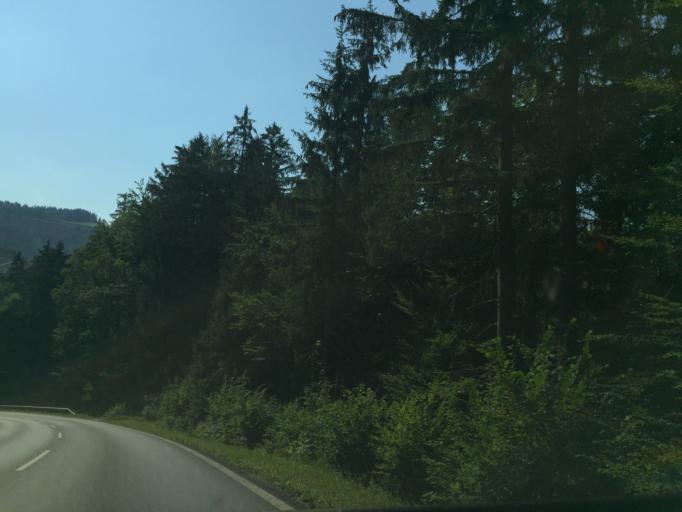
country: AT
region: Styria
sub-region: Politischer Bezirk Deutschlandsberg
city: Aibl
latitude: 46.6497
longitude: 15.2103
